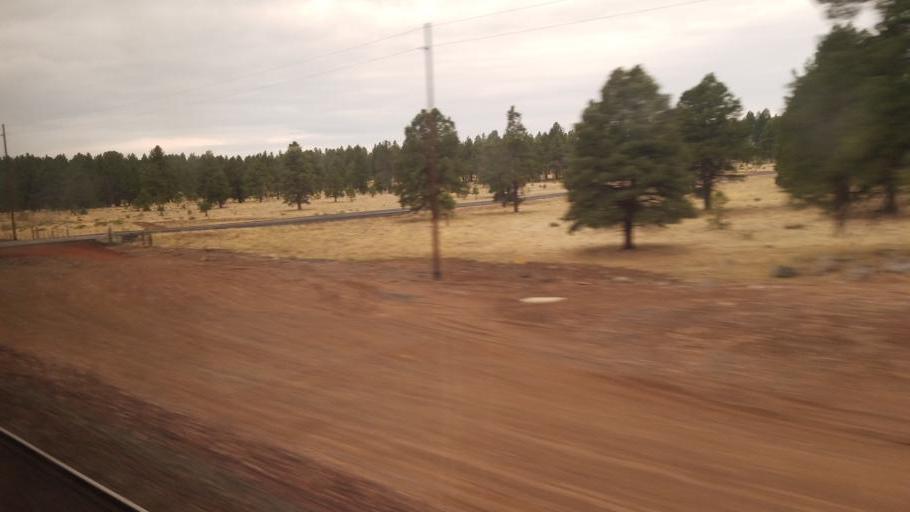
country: US
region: Arizona
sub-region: Coconino County
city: Parks
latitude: 35.2363
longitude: -112.0265
